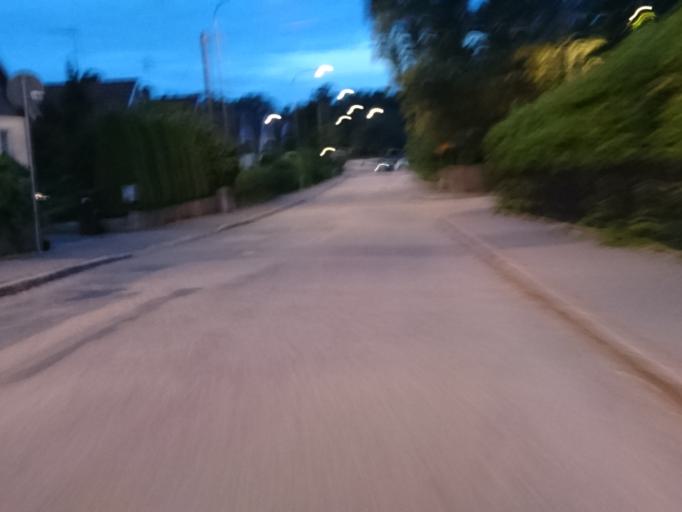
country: SE
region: Stockholm
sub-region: Huddinge Kommun
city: Huddinge
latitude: 59.2760
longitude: 17.9878
